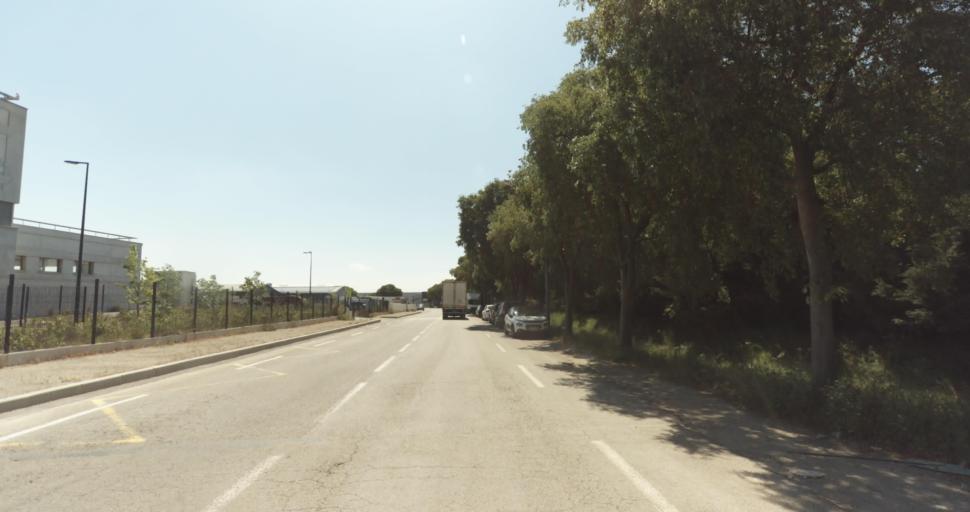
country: FR
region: Languedoc-Roussillon
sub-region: Departement du Gard
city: Milhaud
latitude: 43.8078
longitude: 4.3122
